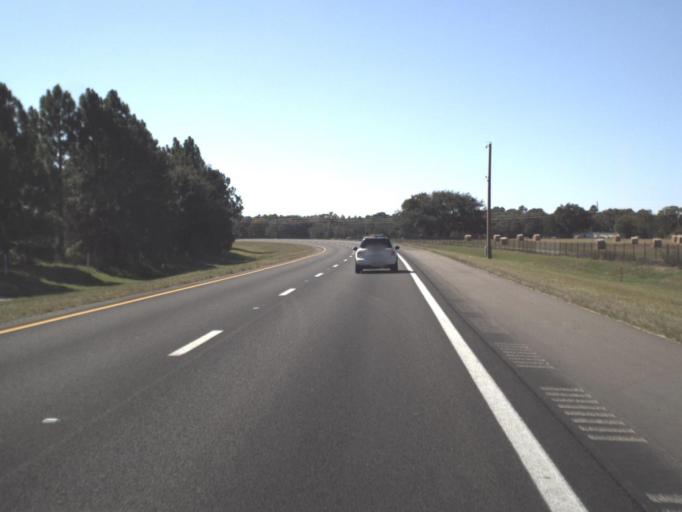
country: US
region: Florida
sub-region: Hernando County
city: Masaryktown
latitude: 28.4557
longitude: -82.4827
